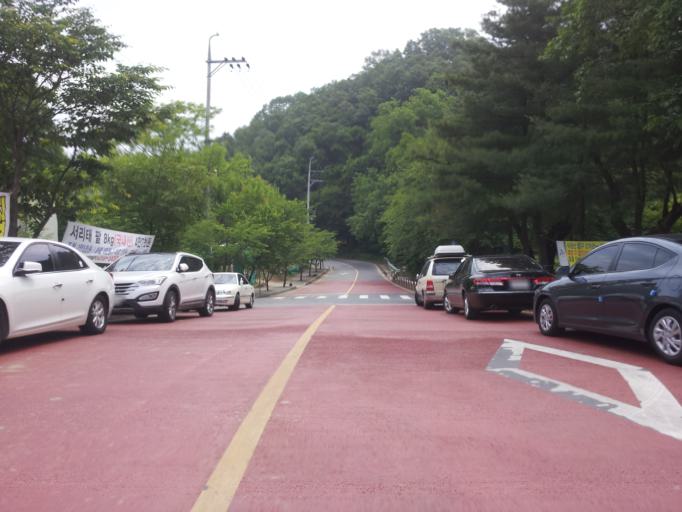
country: KR
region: Daejeon
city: Daejeon
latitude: 36.3303
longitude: 127.4843
